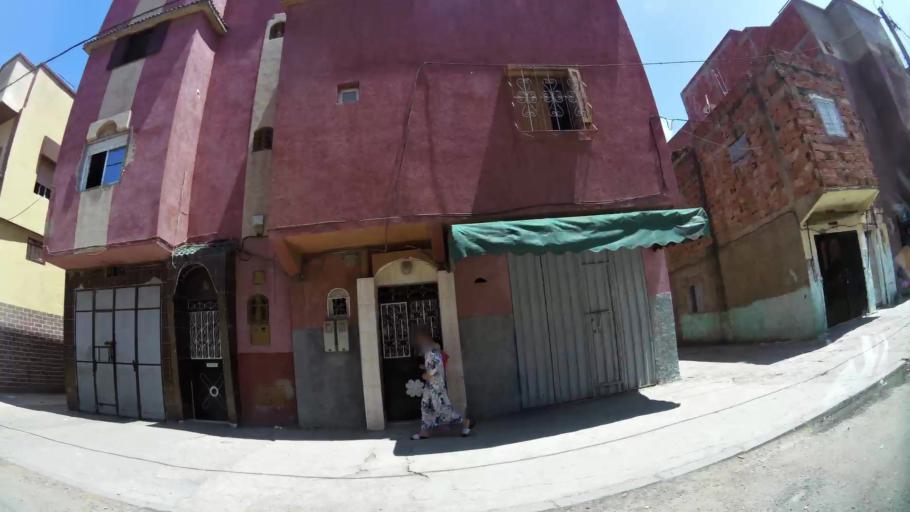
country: MA
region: Gharb-Chrarda-Beni Hssen
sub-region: Kenitra Province
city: Kenitra
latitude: 34.2561
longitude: -6.5471
